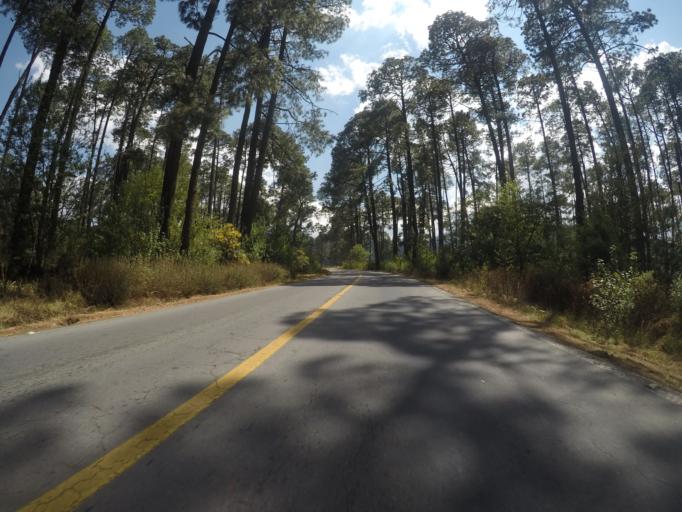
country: MX
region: Mexico
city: Cerro La Calera
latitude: 19.2034
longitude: -99.8101
